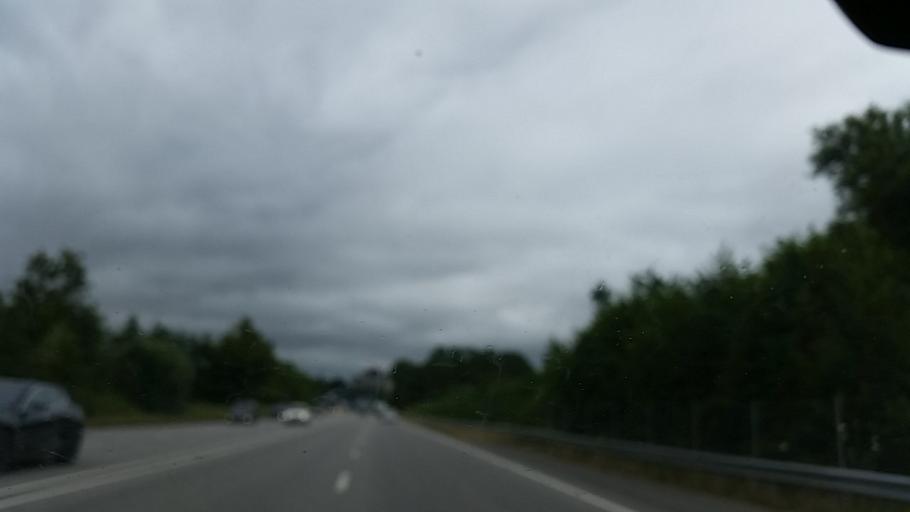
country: DE
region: Schleswig-Holstein
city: Eckernforde
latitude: 54.4680
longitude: 9.8312
